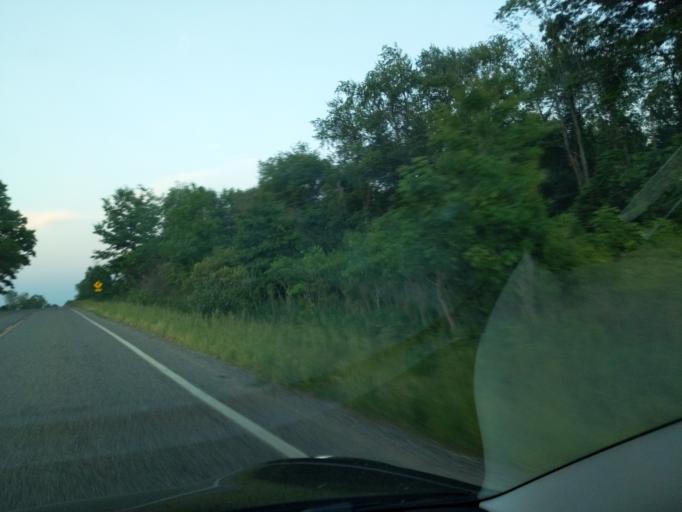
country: US
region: Michigan
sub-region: Barry County
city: Nashville
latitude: 42.5383
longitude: -85.0566
